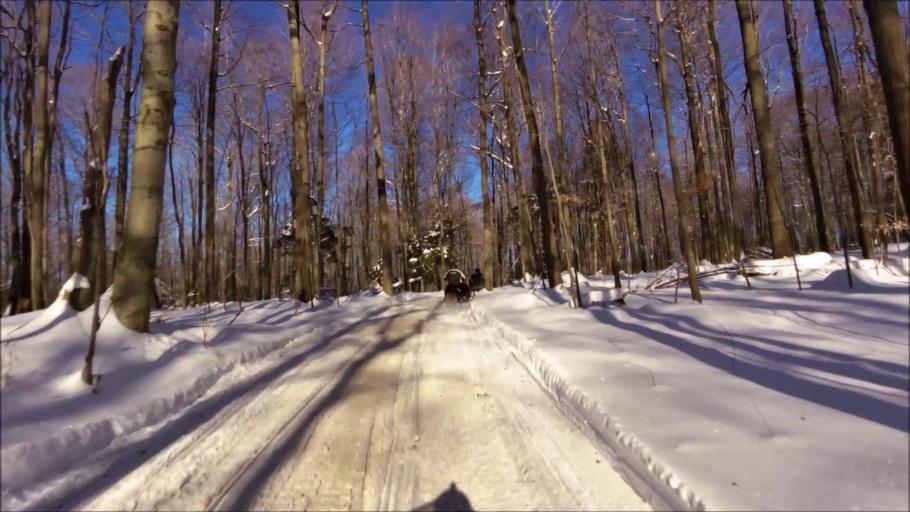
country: US
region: New York
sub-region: Chautauqua County
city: Mayville
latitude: 42.2777
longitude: -79.4131
